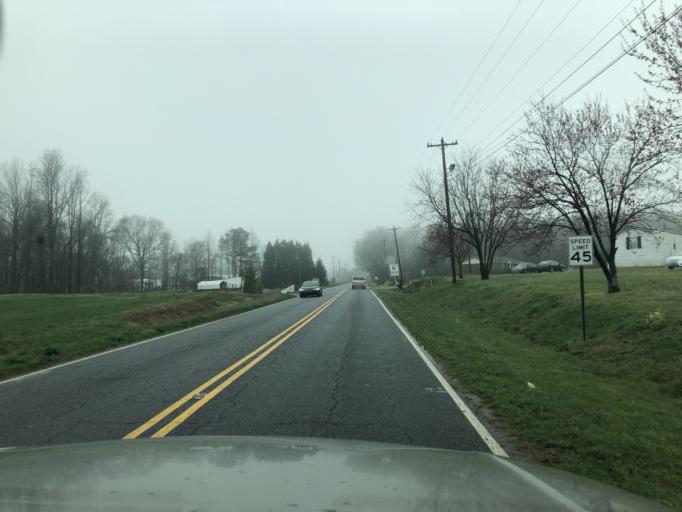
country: US
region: North Carolina
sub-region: Gaston County
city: Cherryville
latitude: 35.3668
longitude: -81.4182
